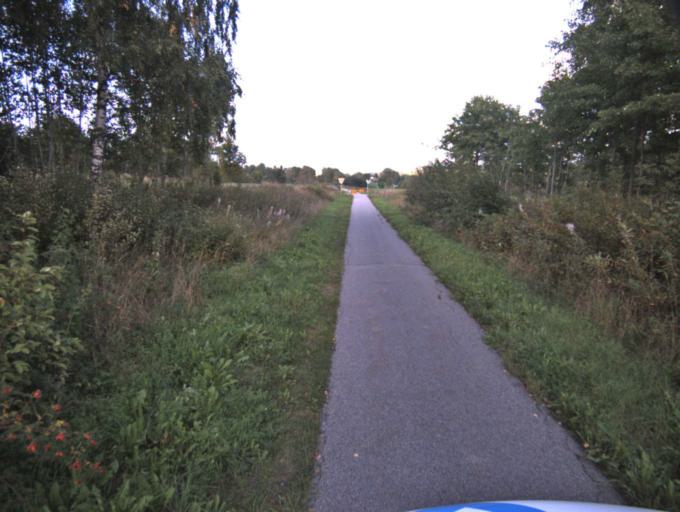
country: SE
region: Vaestra Goetaland
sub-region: Ulricehamns Kommun
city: Ulricehamn
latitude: 57.9145
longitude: 13.4813
